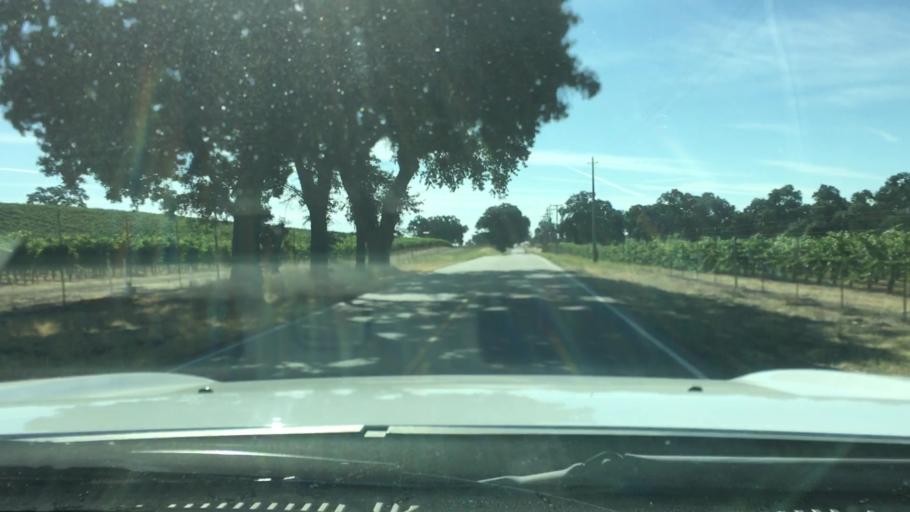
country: US
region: California
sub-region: San Luis Obispo County
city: Atascadero
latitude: 35.5548
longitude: -120.6209
